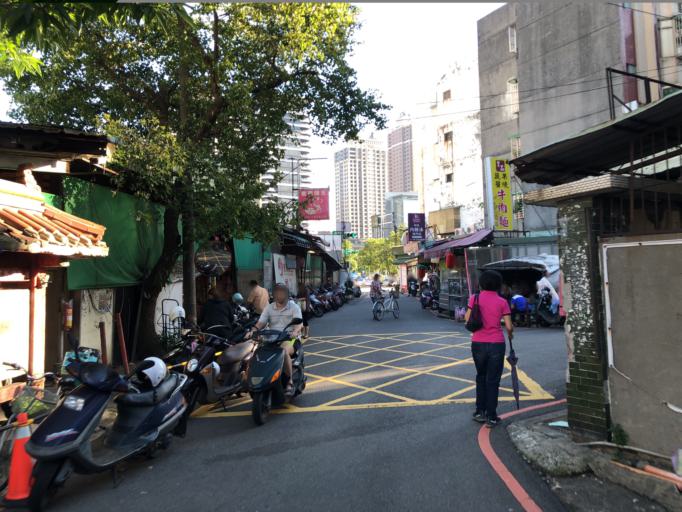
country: TW
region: Taiwan
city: Taoyuan City
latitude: 25.0196
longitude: 121.3006
